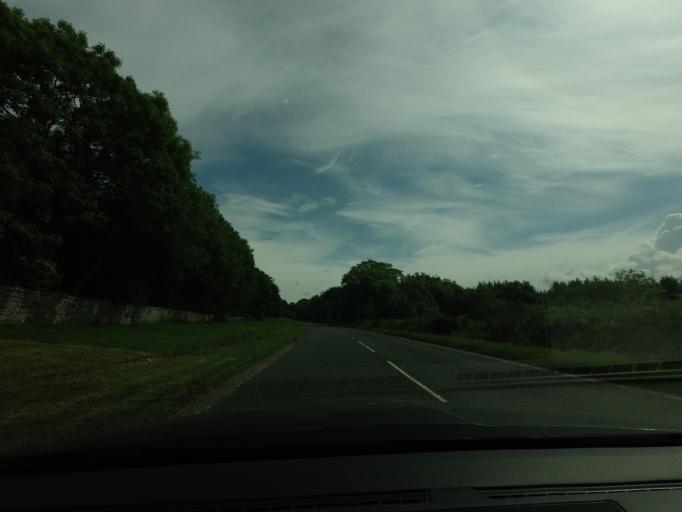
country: GB
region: Scotland
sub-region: Aberdeenshire
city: Mintlaw
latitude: 57.5249
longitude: -2.0355
